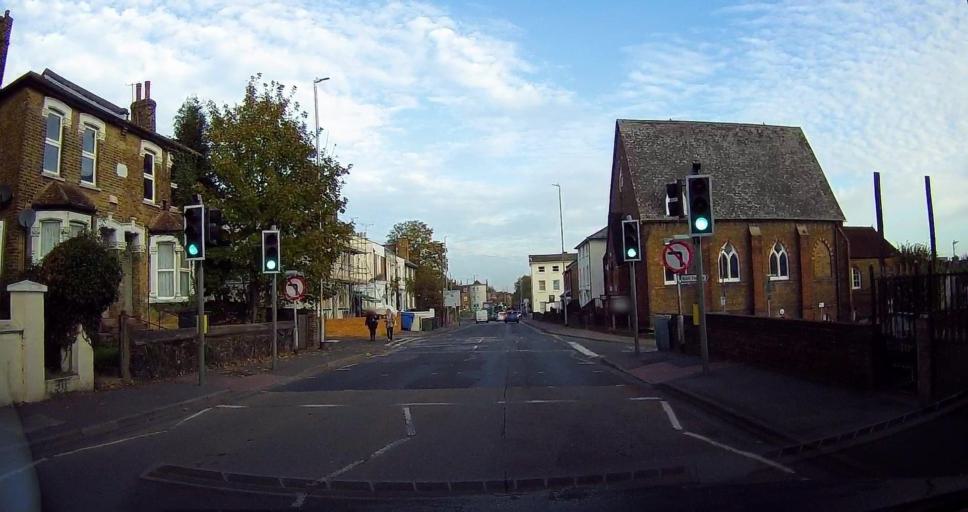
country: GB
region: England
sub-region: Kent
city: Dartford
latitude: 51.4438
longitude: 0.2125
